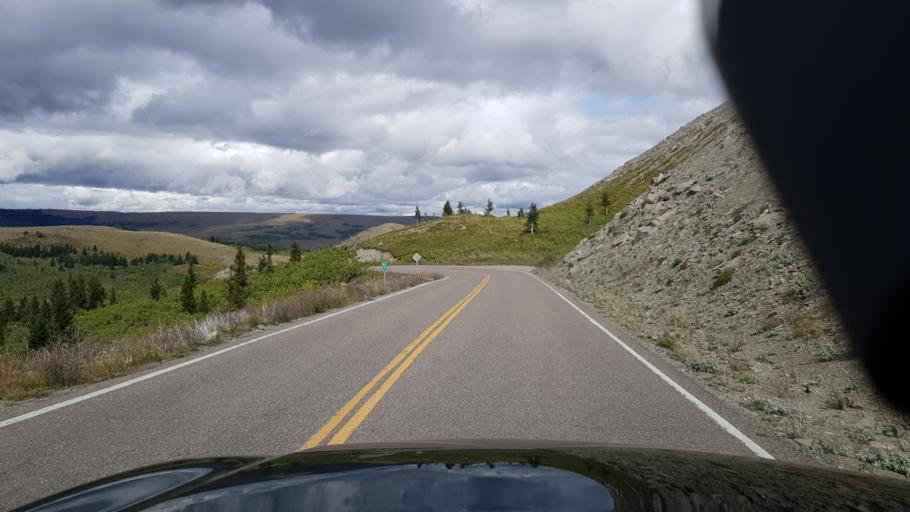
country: US
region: Montana
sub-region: Glacier County
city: South Browning
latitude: 48.5407
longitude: -113.3044
